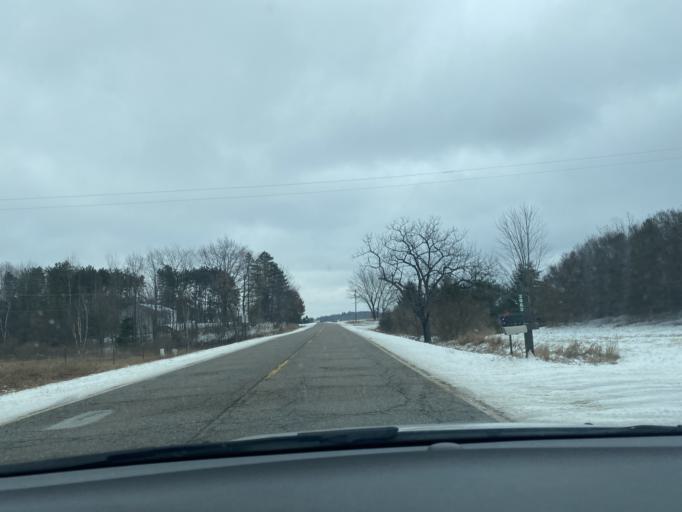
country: US
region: Michigan
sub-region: Lapeer County
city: North Branch
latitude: 43.2065
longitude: -83.2357
